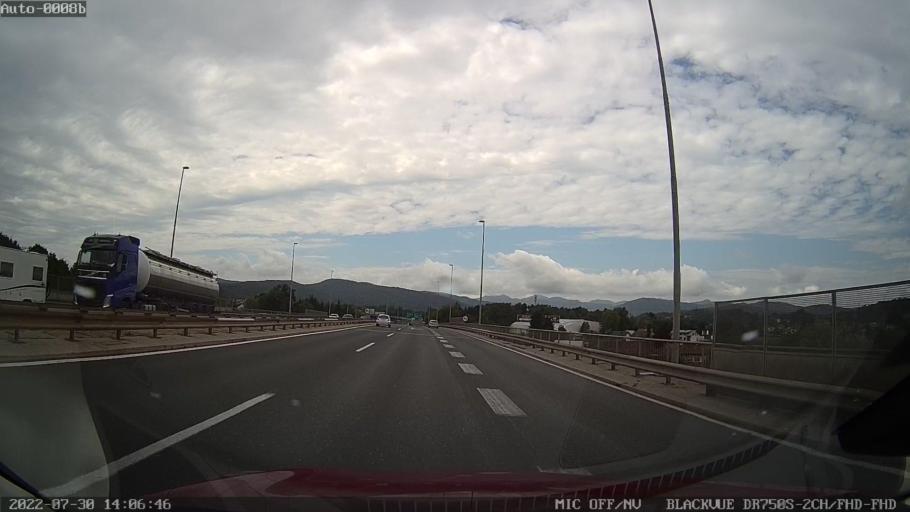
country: SI
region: Brezovica
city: Vnanje Gorice
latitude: 46.0414
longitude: 14.4531
